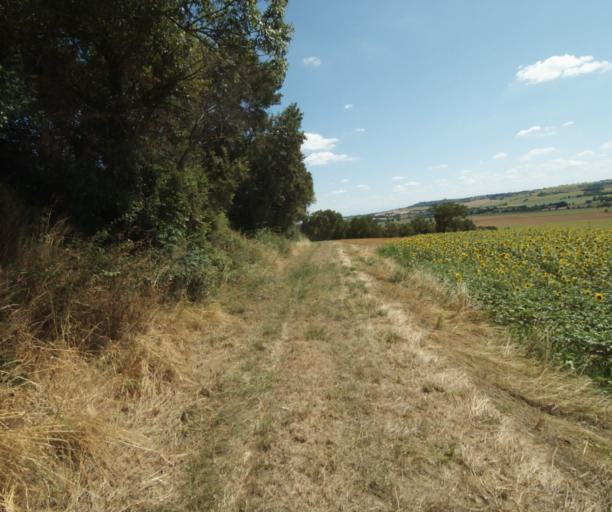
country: FR
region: Midi-Pyrenees
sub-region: Departement de la Haute-Garonne
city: Saint-Felix-Lauragais
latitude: 43.4907
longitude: 1.8927
